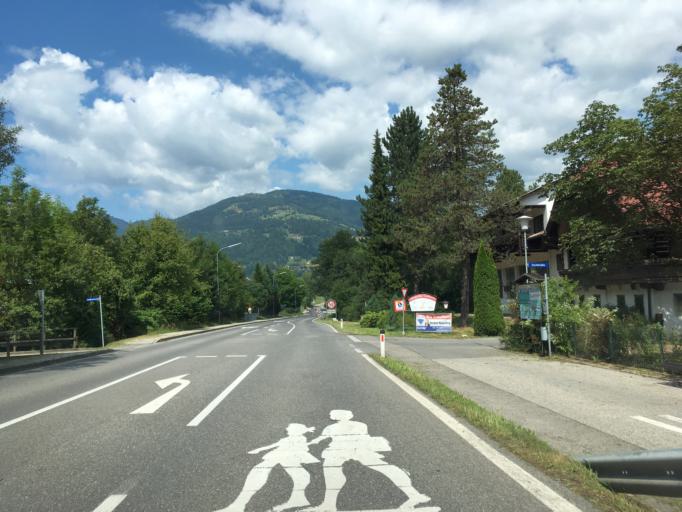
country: AT
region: Carinthia
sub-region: Politischer Bezirk Spittal an der Drau
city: Radenthein
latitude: 46.7910
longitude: 13.7270
